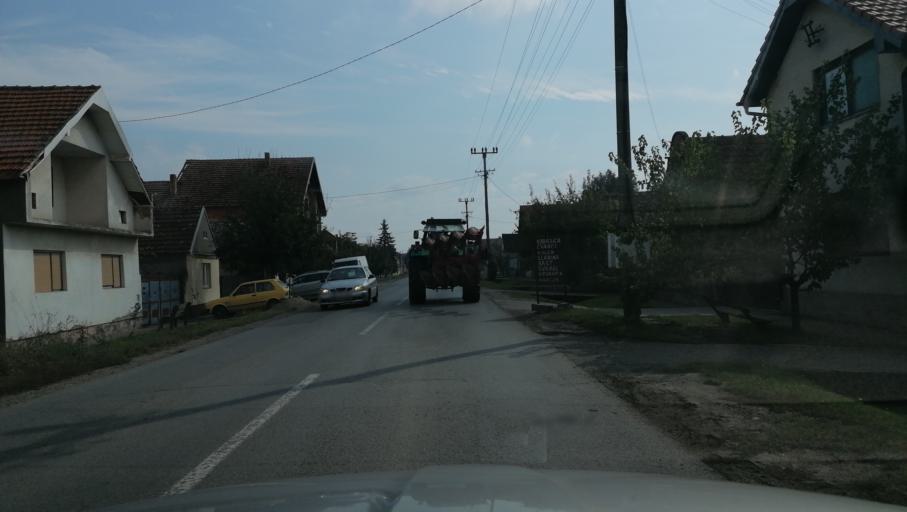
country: RS
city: Ravnje
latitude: 45.0275
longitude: 19.3937
